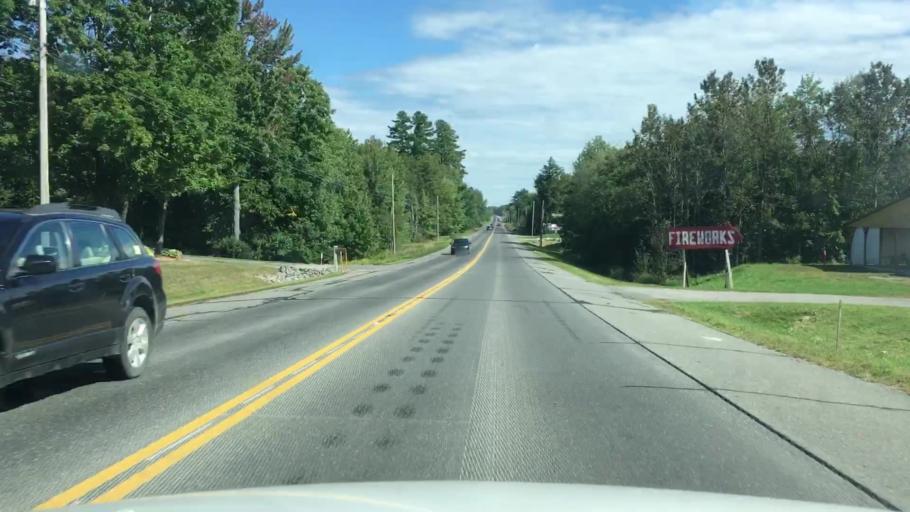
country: US
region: Maine
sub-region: Penobscot County
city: Corinna
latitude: 44.8844
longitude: -69.2779
